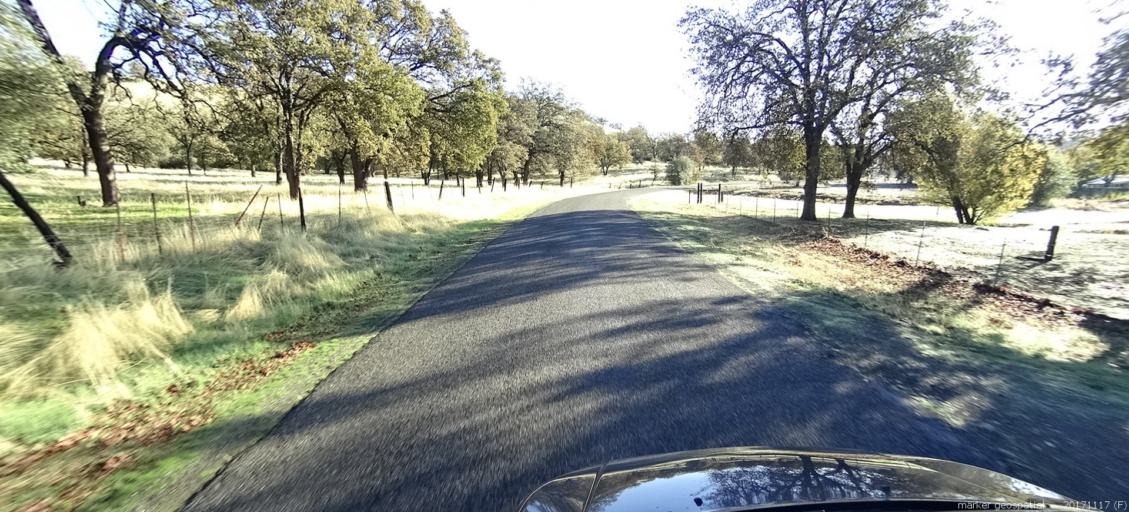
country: US
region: California
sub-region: Shasta County
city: Cottonwood
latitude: 40.4026
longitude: -122.1476
